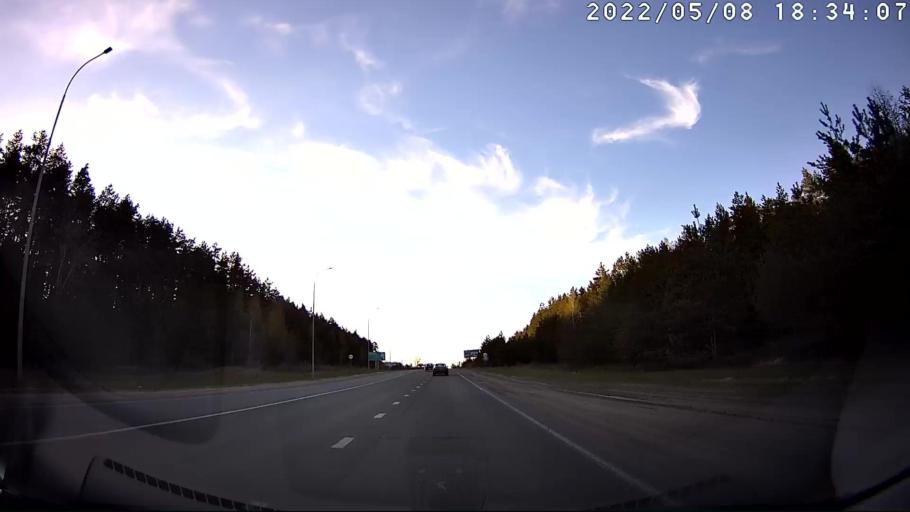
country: RU
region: Mariy-El
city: Volzhsk
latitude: 55.8971
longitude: 48.3564
